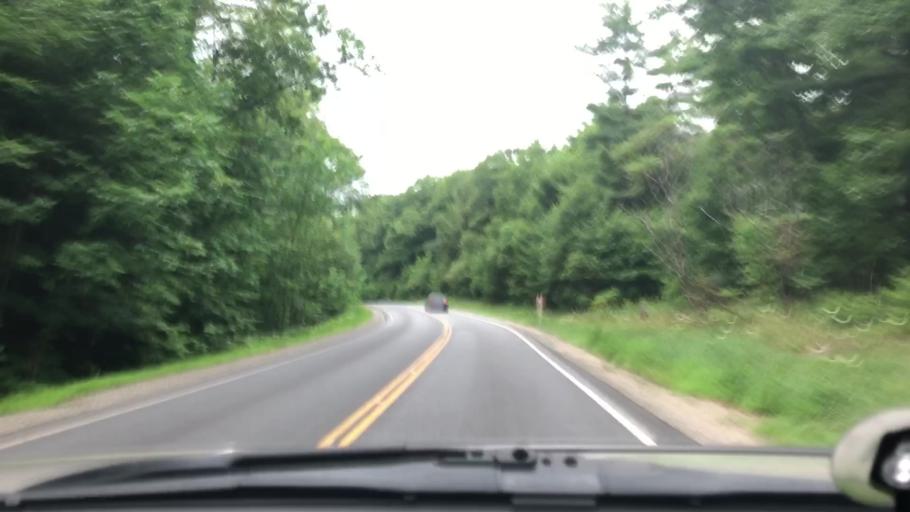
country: US
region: New York
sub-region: Saratoga County
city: Corinth
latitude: 43.2030
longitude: -73.7674
